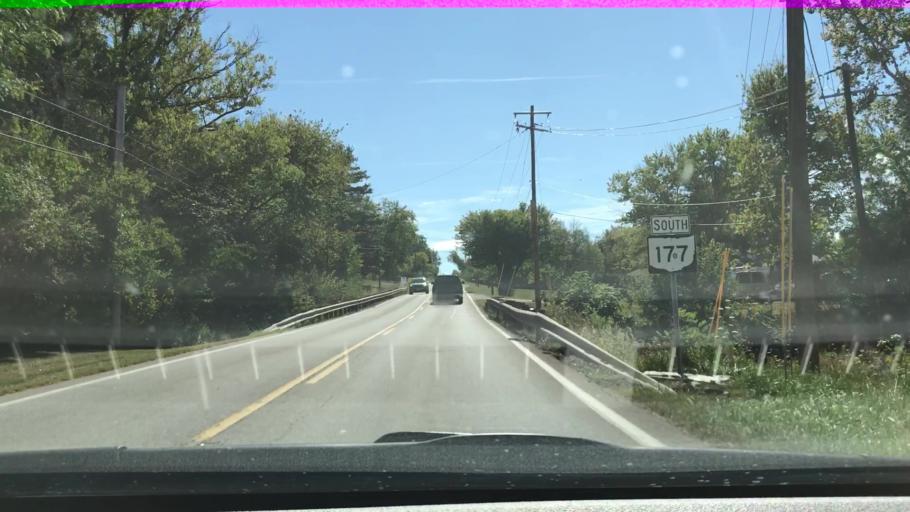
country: US
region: Ohio
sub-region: Butler County
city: Hamilton
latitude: 39.4532
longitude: -84.6228
